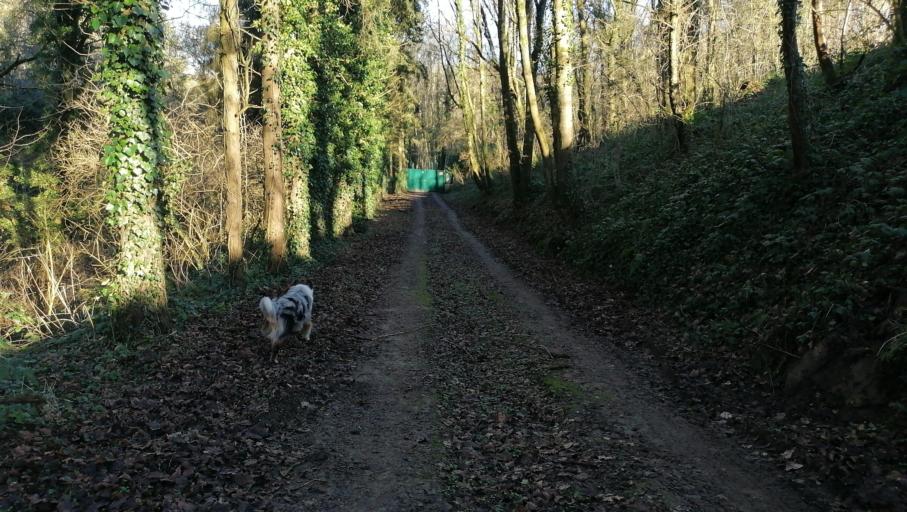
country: FR
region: Nord-Pas-de-Calais
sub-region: Departement du Nord
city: Recquignies
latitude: 50.2060
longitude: 4.0567
